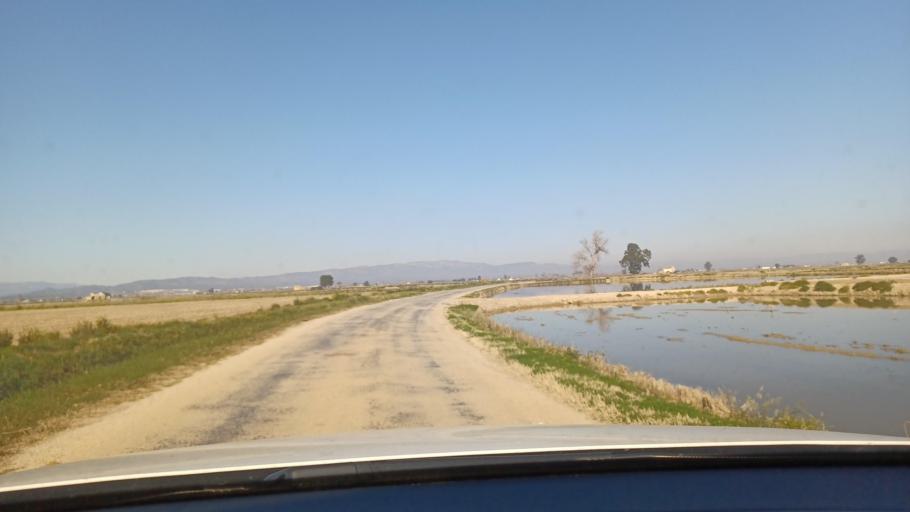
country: ES
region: Catalonia
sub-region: Provincia de Tarragona
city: Deltebre
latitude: 40.6901
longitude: 0.6515
